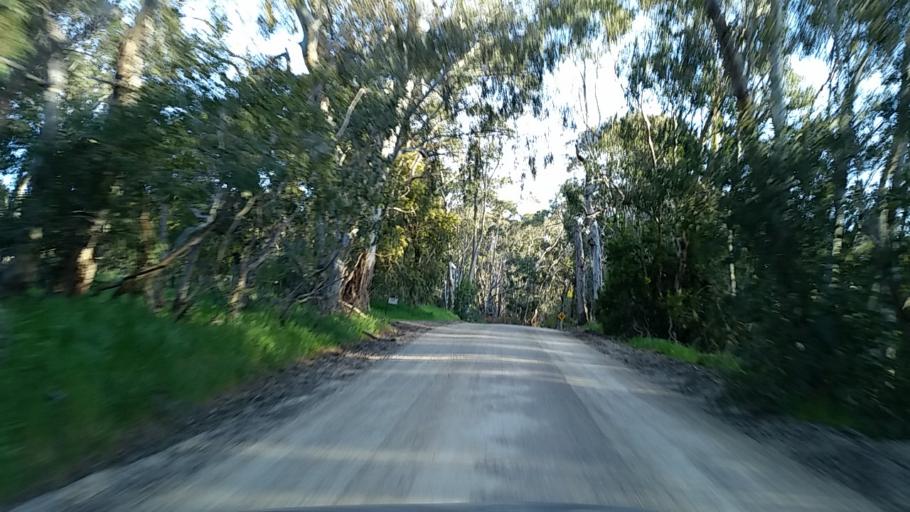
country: AU
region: South Australia
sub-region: Mount Barker
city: Meadows
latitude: -35.2720
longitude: 138.7016
